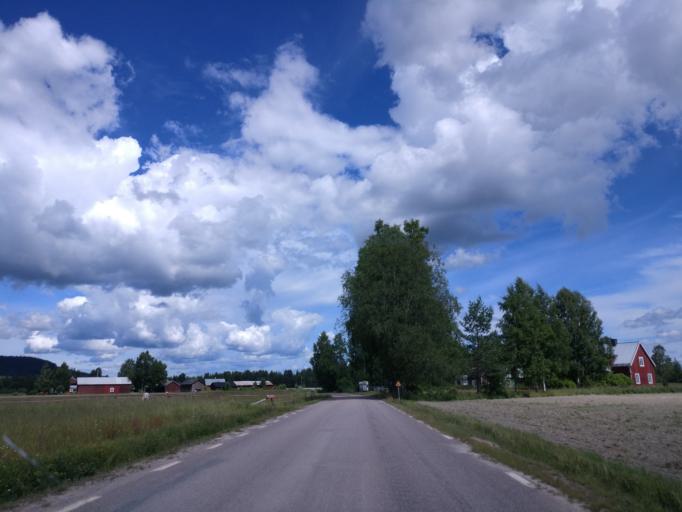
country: SE
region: Vaermland
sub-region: Hagfors Kommun
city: Ekshaerad
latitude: 60.0444
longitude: 13.4931
